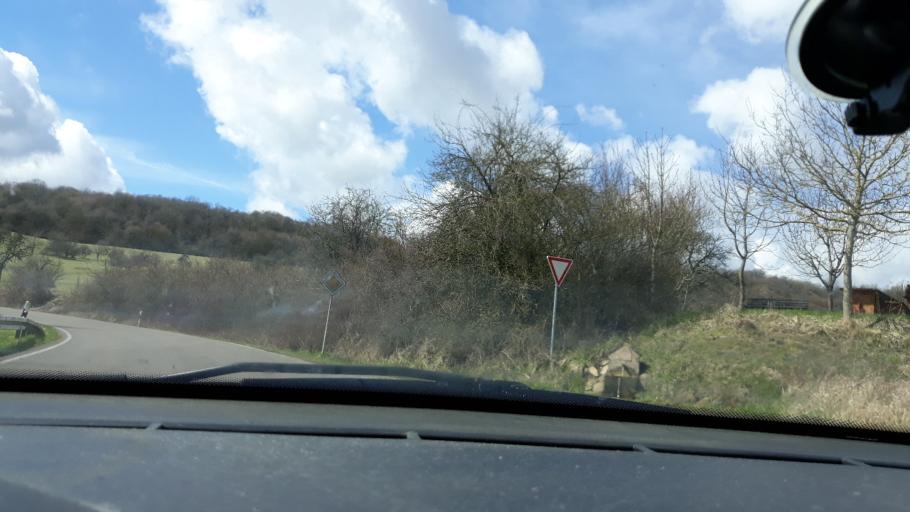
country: DE
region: Saarland
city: Blieskastel
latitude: 49.1986
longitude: 7.2323
